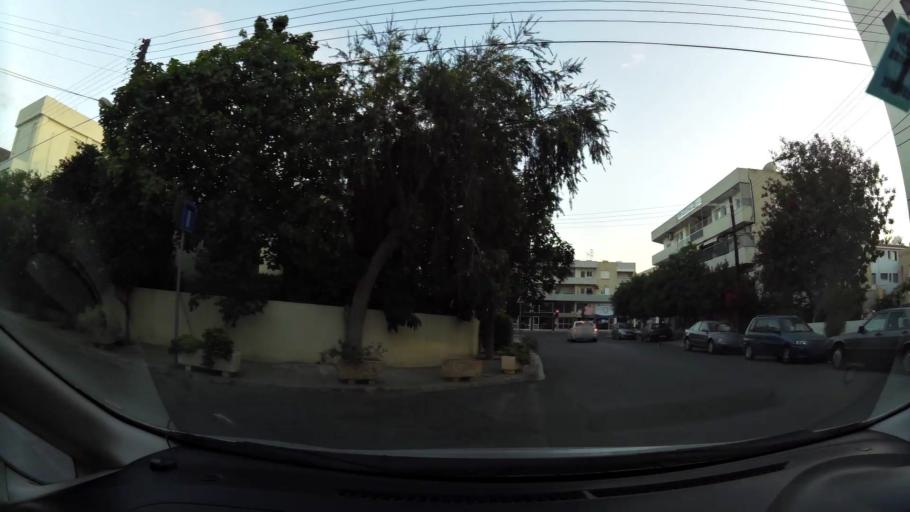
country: CY
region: Lefkosia
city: Nicosia
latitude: 35.1495
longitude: 33.3884
